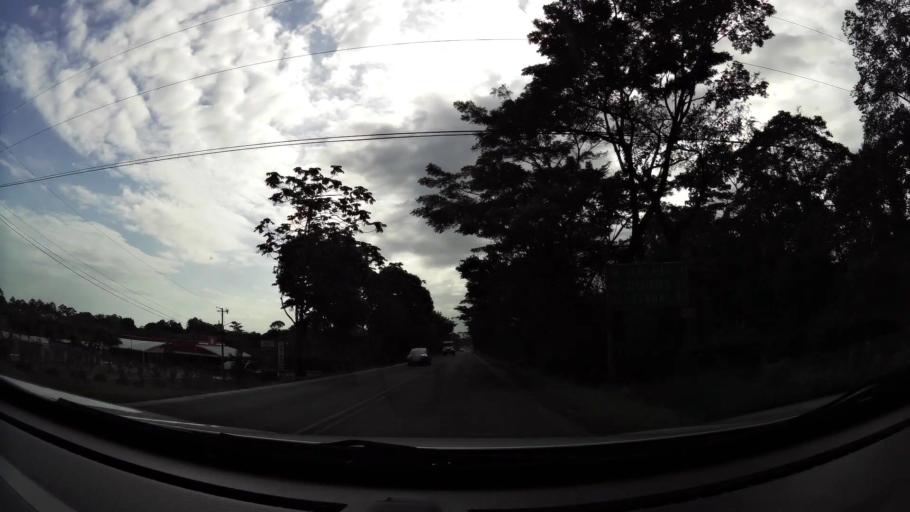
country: CR
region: Limon
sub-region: Canton de Guacimo
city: Guacimo
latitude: 10.2051
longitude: -83.6830
